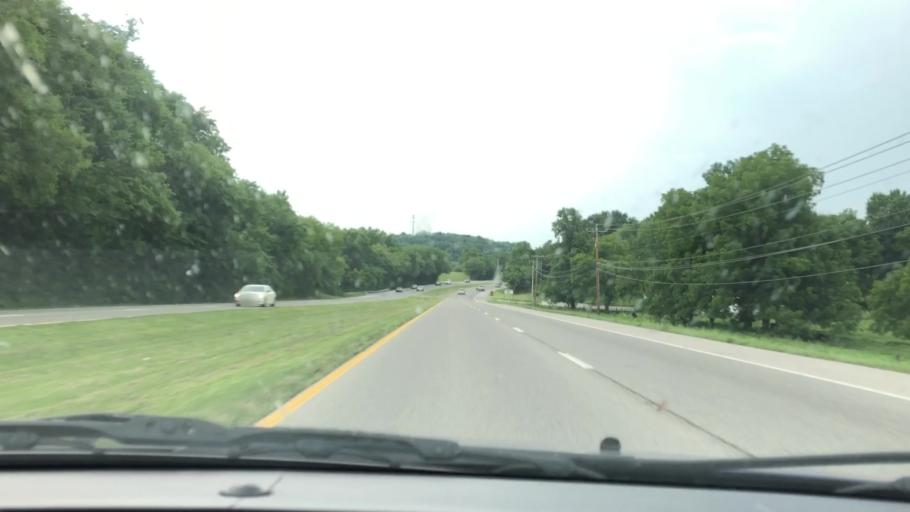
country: US
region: Tennessee
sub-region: Maury County
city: Columbia
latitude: 35.6780
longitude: -86.9992
